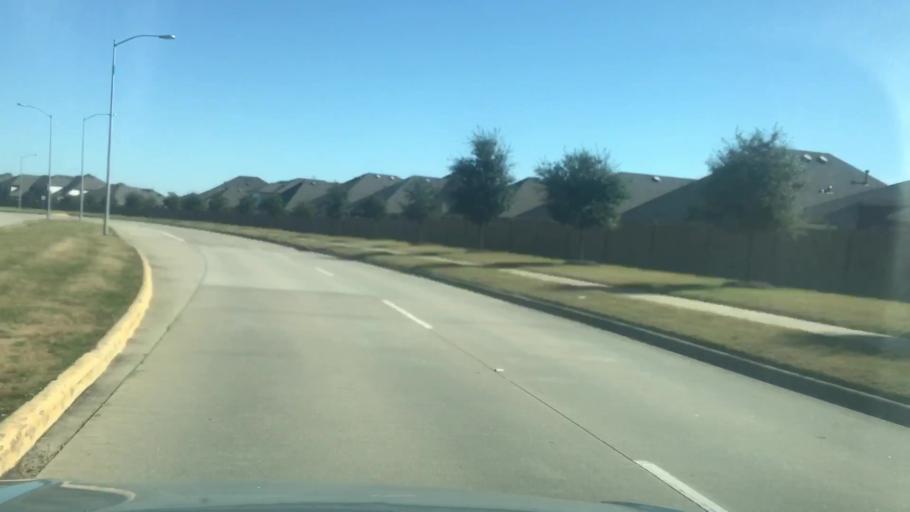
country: US
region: Texas
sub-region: Fort Bend County
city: Cinco Ranch
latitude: 29.7344
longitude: -95.8060
